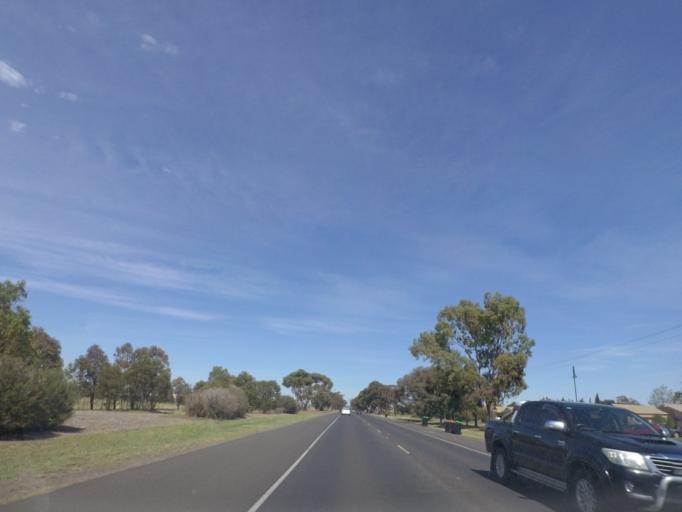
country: AU
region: Victoria
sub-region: Melton
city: Brookfield
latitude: -37.6859
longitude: 144.5458
